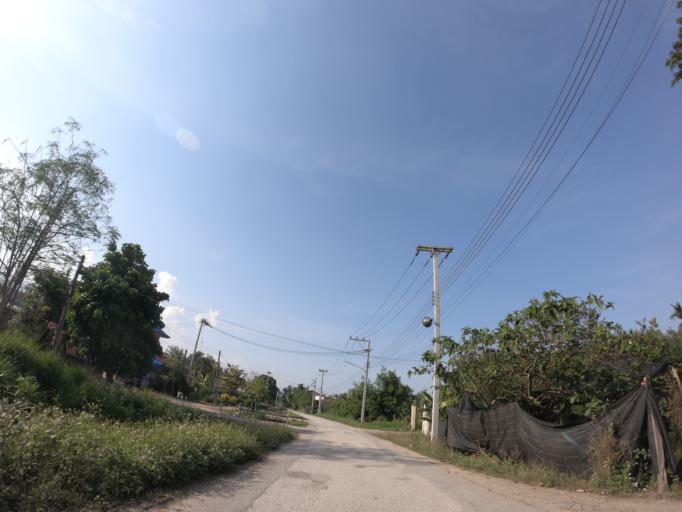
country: TH
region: Chiang Mai
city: Chiang Mai
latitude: 18.8274
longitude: 98.9927
